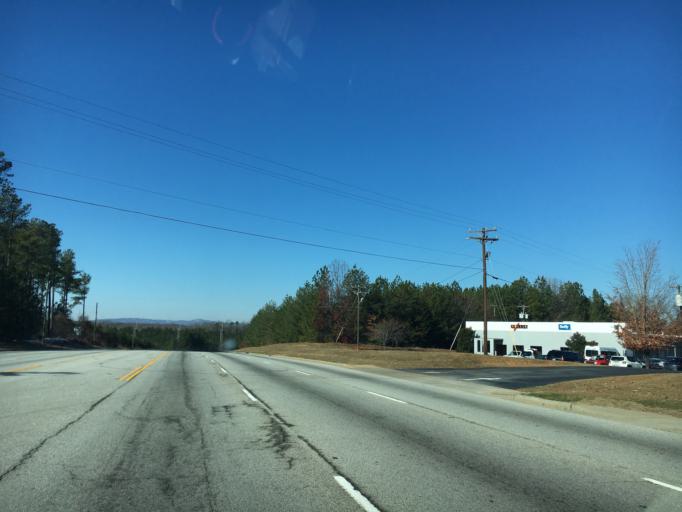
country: US
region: South Carolina
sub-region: Greenville County
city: Greer
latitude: 34.8772
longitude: -82.2272
